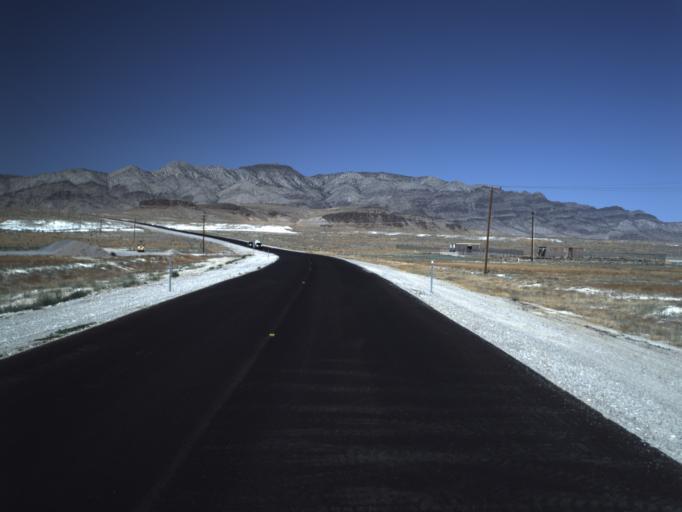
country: US
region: Utah
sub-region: Beaver County
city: Milford
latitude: 39.0820
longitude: -113.4918
